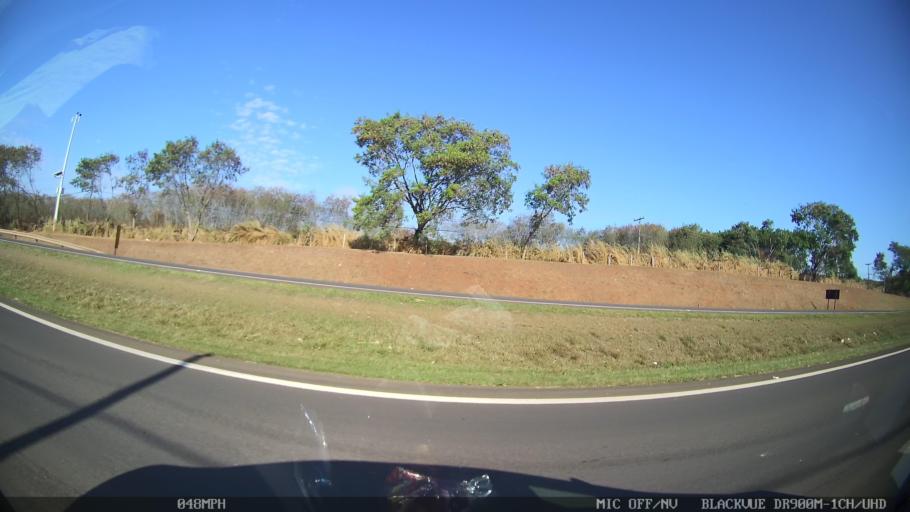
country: BR
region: Sao Paulo
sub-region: Piracicaba
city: Piracicaba
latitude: -22.6661
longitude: -47.6210
